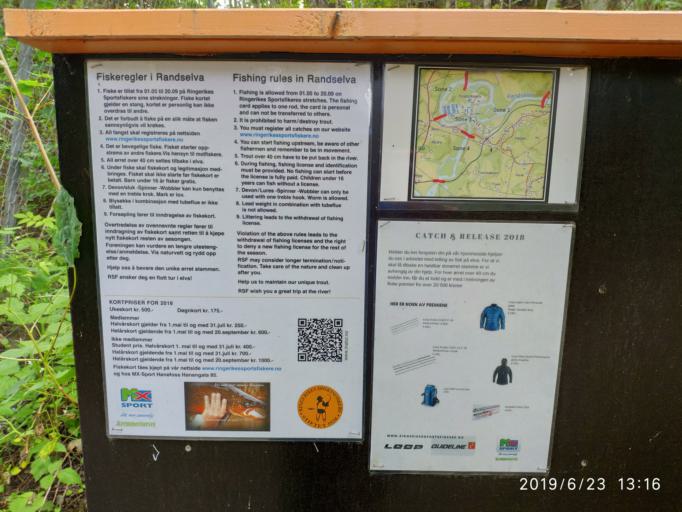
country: NO
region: Buskerud
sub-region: Ringerike
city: Honefoss
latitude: 60.1892
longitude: 10.3060
